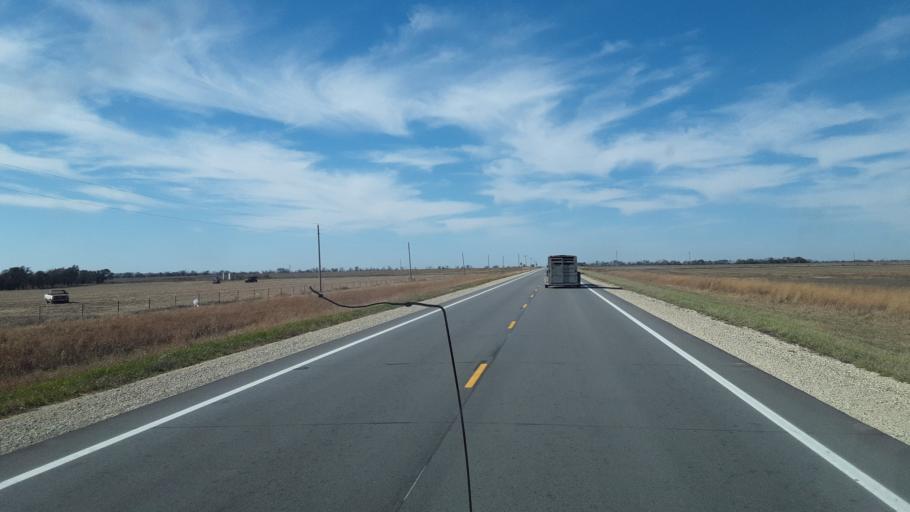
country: US
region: Kansas
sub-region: Marion County
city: Marion
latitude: 38.3629
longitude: -96.8875
